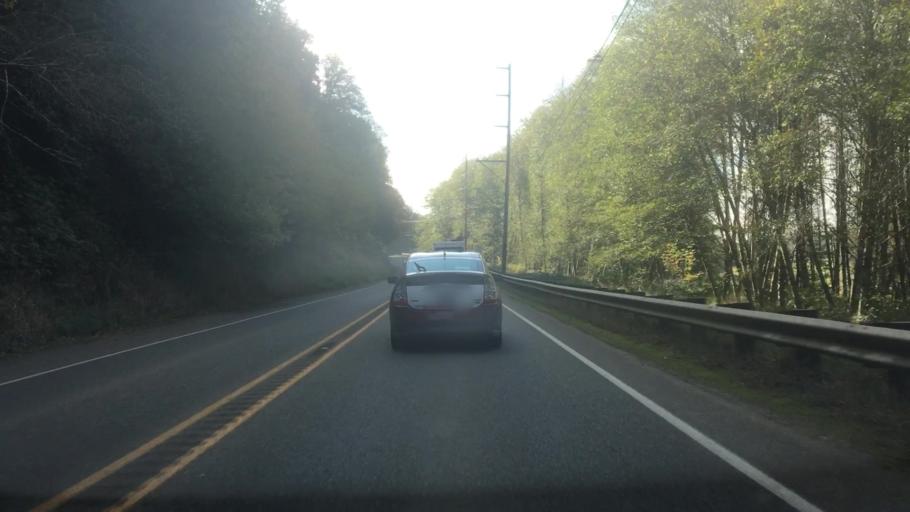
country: US
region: Washington
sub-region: Grays Harbor County
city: Montesano
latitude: 46.9576
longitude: -123.6060
